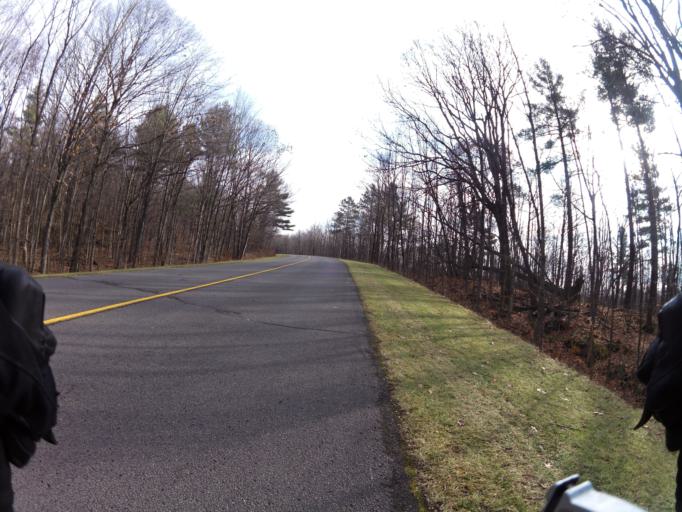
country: CA
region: Quebec
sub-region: Outaouais
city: Gatineau
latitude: 45.4668
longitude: -75.8138
